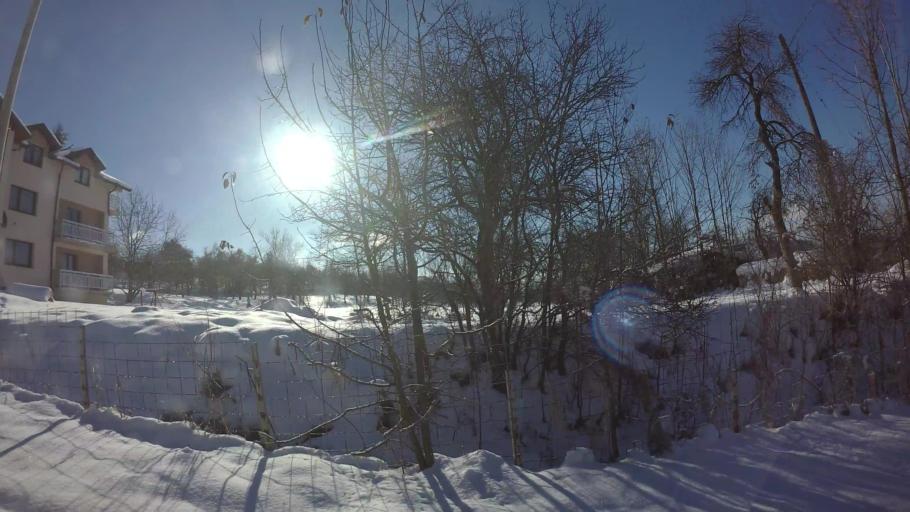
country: BA
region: Federation of Bosnia and Herzegovina
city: Kobilja Glava
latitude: 43.8961
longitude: 18.4170
